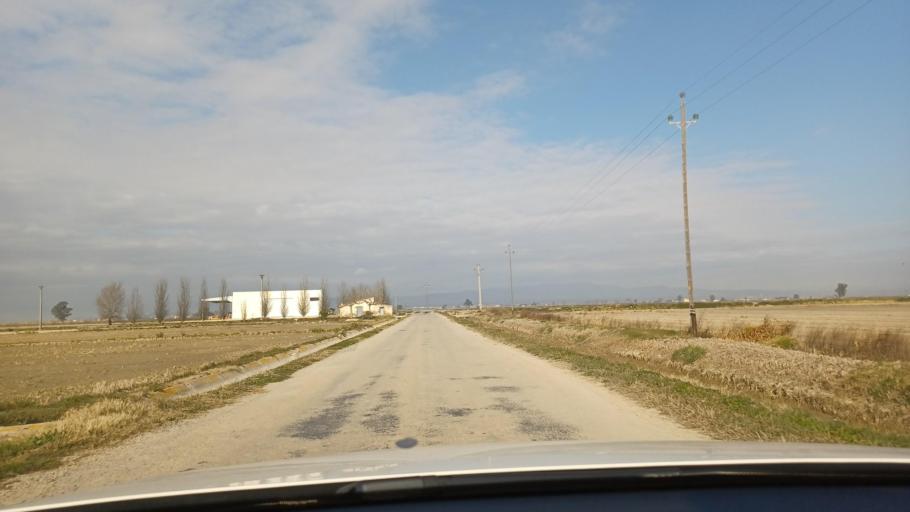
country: ES
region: Catalonia
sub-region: Provincia de Tarragona
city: Deltebre
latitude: 40.6802
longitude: 0.6583
